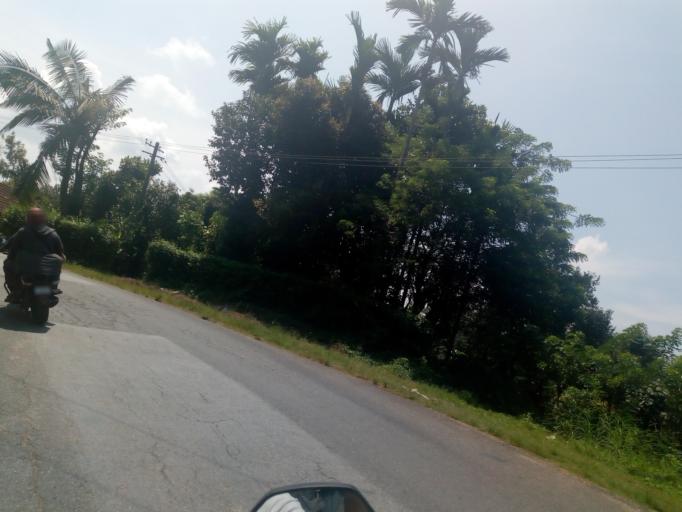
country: IN
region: Karnataka
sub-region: Kodagu
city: Ponnampet
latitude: 12.0974
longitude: 75.9365
